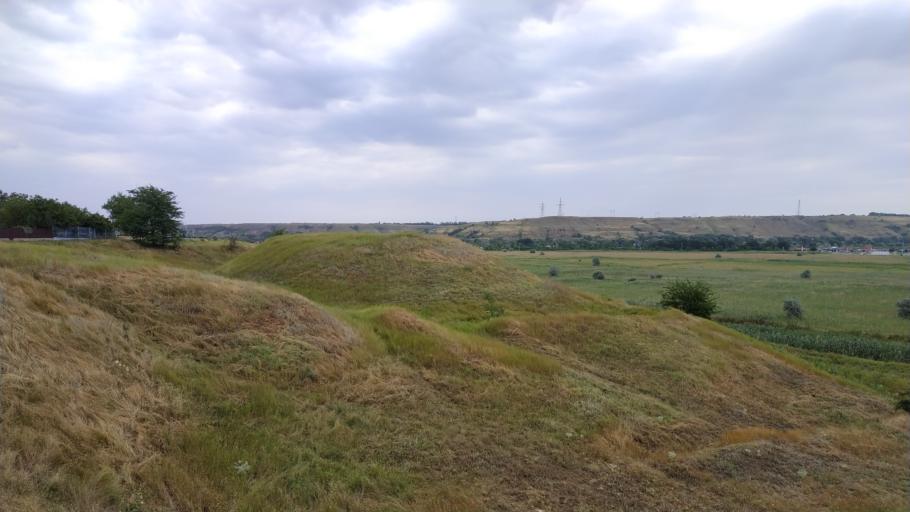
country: RU
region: Krasnodarskiy
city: Krasnaya Polyana
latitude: 45.0253
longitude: 41.1042
